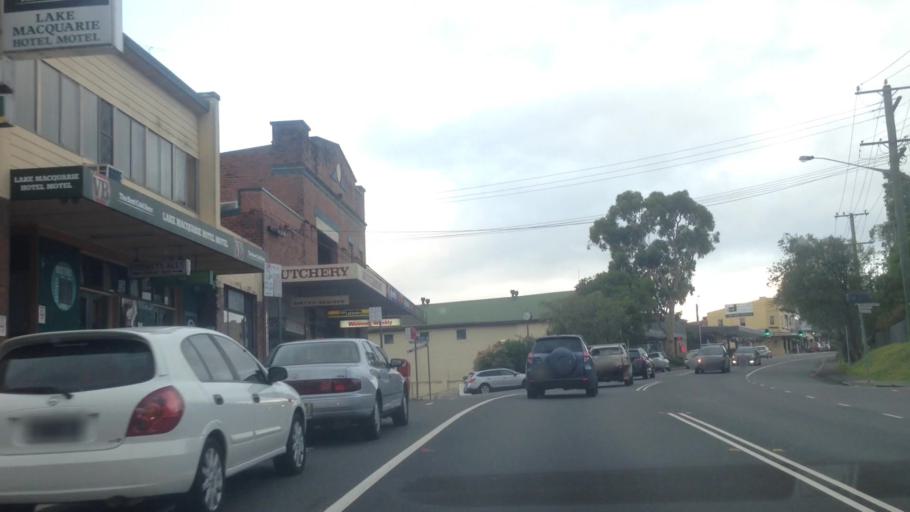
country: AU
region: New South Wales
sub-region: Lake Macquarie Shire
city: Dora Creek
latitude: -33.1086
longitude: 151.4873
